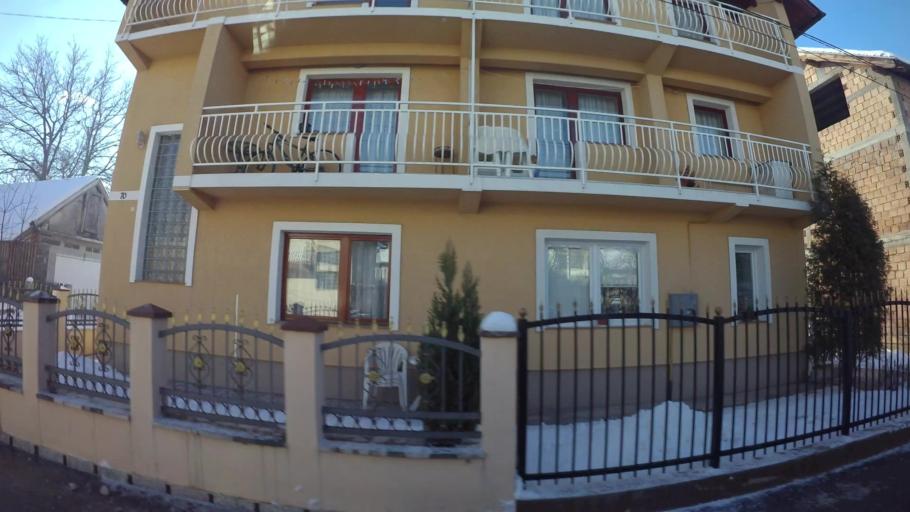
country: BA
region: Federation of Bosnia and Herzegovina
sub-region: Kanton Sarajevo
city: Sarajevo
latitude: 43.8070
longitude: 18.3157
